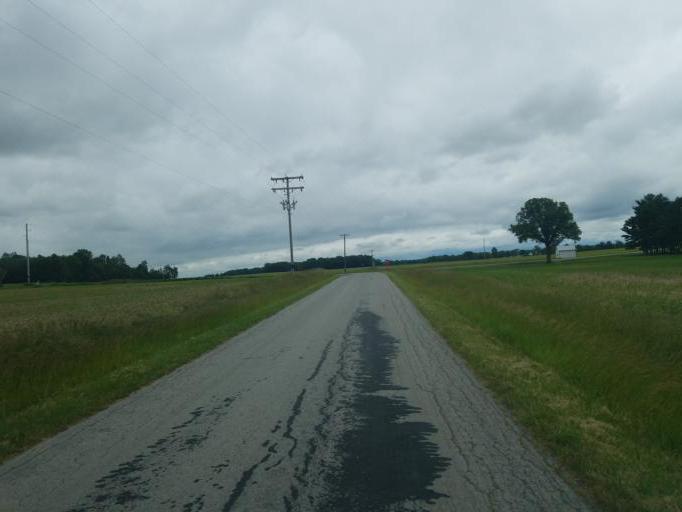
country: US
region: Ohio
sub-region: Crawford County
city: Bucyrus
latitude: 40.7619
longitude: -82.9182
